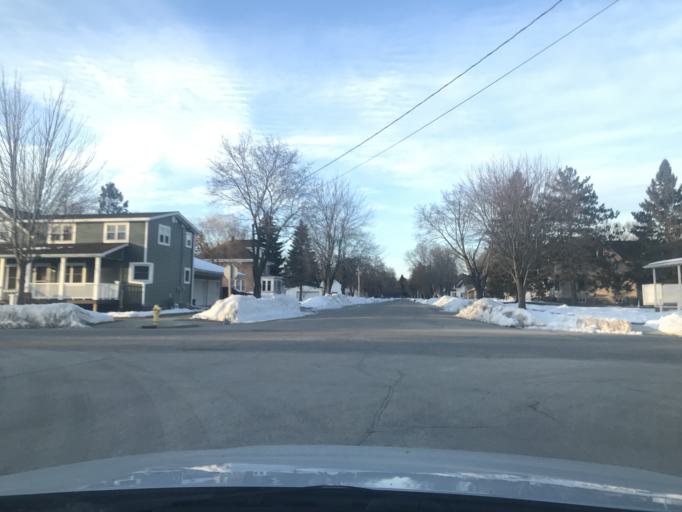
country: US
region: Wisconsin
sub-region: Marinette County
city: Peshtigo
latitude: 45.0549
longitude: -87.7402
